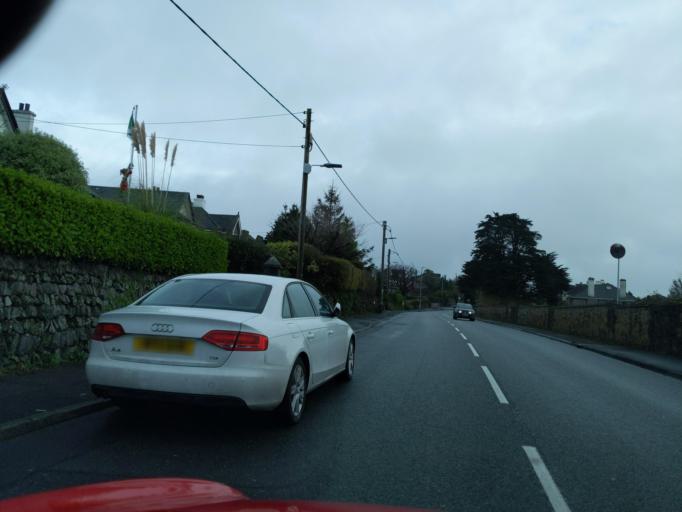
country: GB
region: England
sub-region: Devon
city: Plympton
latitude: 50.3867
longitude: -4.0448
